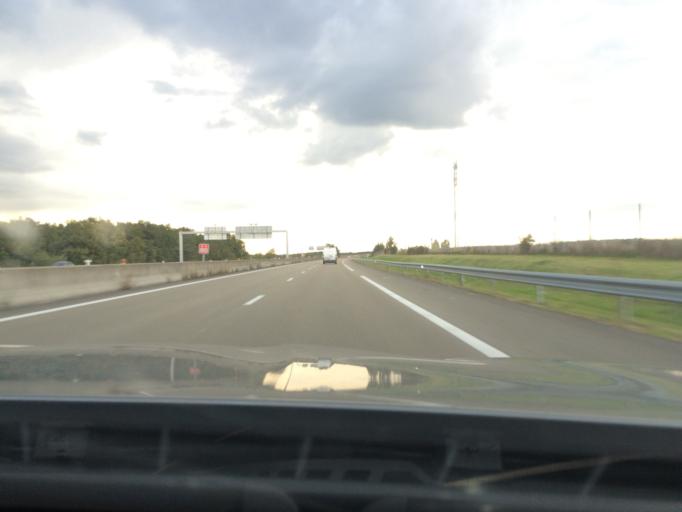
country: FR
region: Ile-de-France
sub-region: Departement de Seine-et-Marne
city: Souppes-sur-Loing
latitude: 48.2190
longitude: 2.7711
